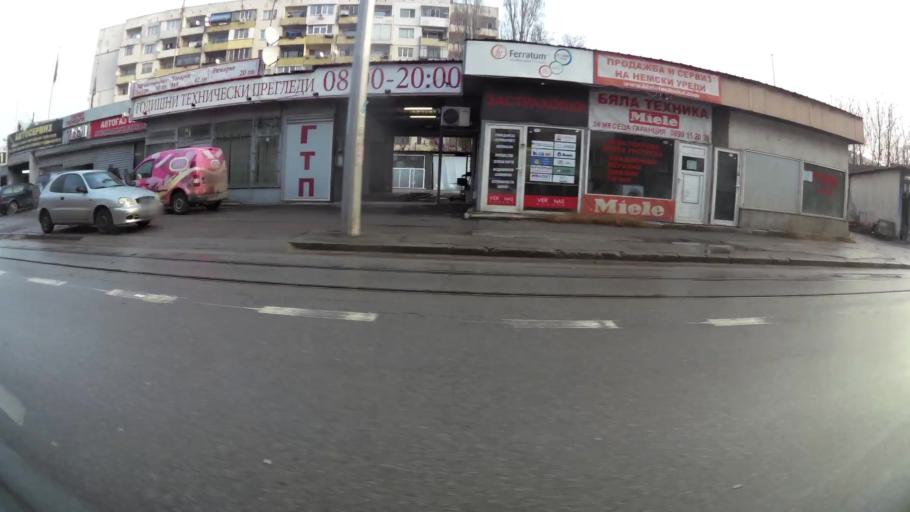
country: BG
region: Sofia-Capital
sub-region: Stolichna Obshtina
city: Sofia
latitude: 42.7330
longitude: 23.3111
